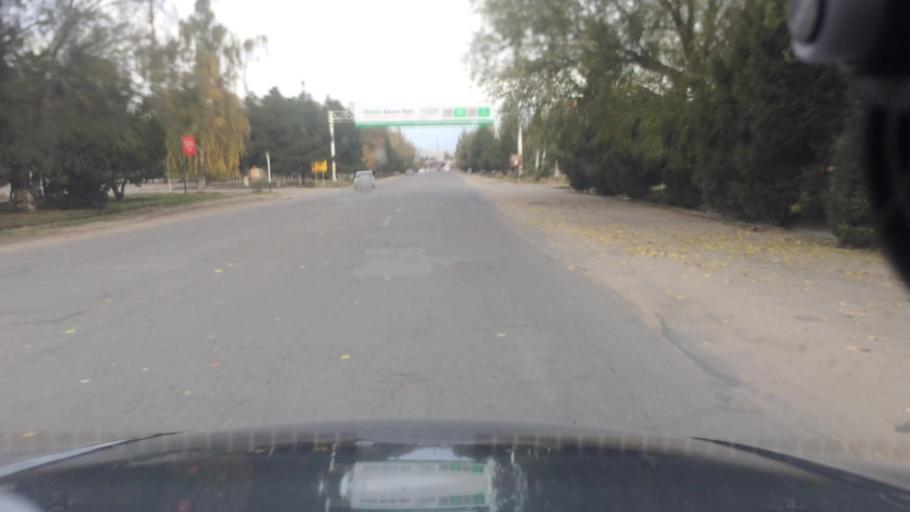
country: KG
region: Ysyk-Koel
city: Karakol
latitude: 42.4962
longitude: 78.3914
